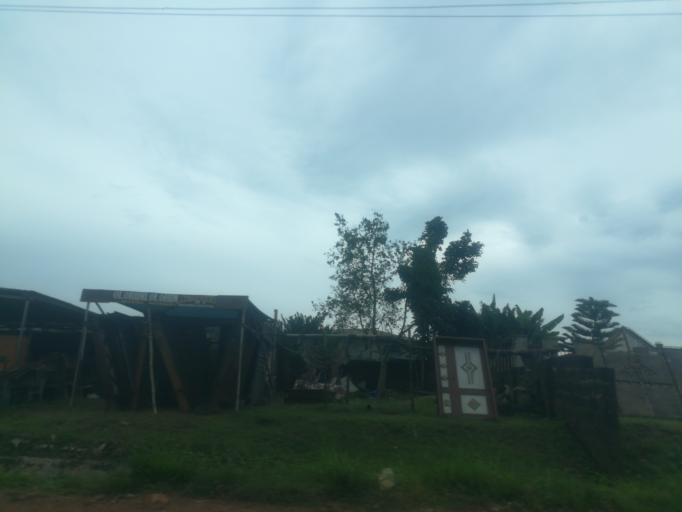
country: NG
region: Oyo
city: Egbeda
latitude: 7.3832
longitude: 3.9909
